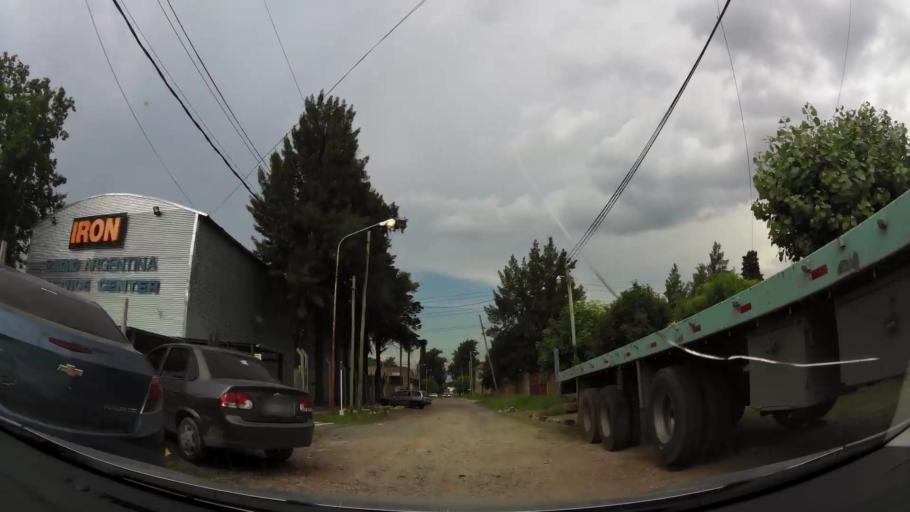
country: AR
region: Buenos Aires
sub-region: Partido de Tigre
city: Tigre
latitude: -34.4838
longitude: -58.6184
